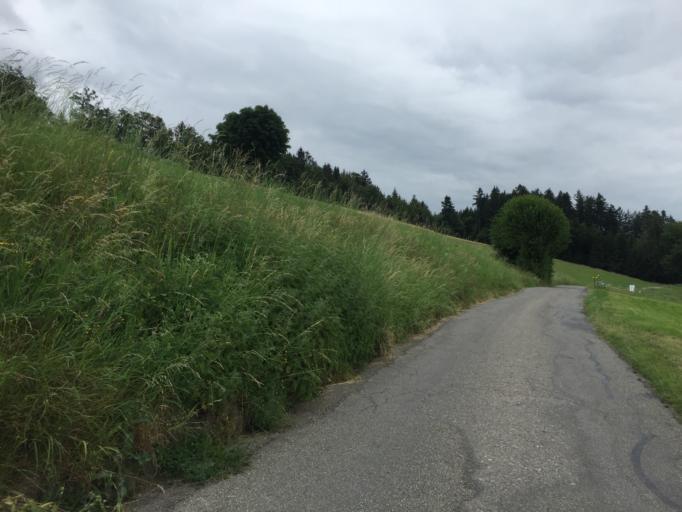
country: CH
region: Bern
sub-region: Bern-Mittelland District
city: Stettlen
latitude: 46.9497
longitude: 7.5208
